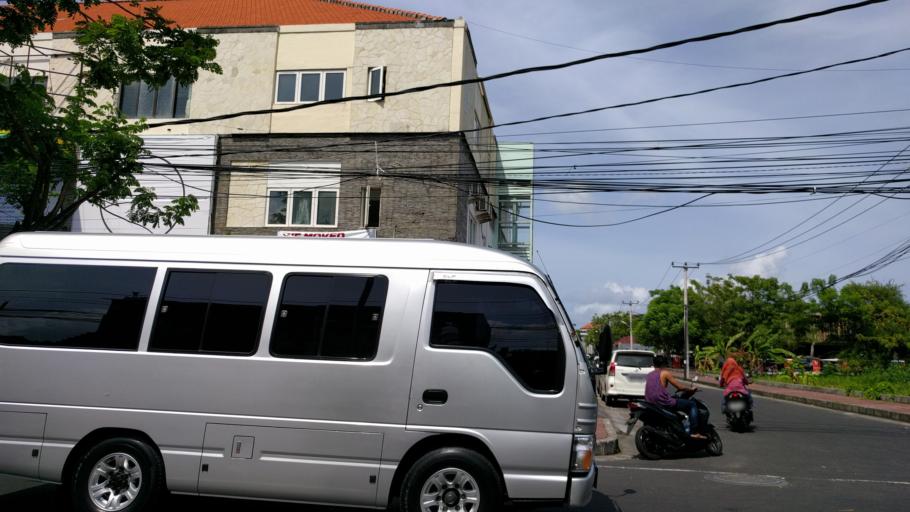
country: ID
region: Bali
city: Kuta
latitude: -8.7048
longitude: 115.1769
